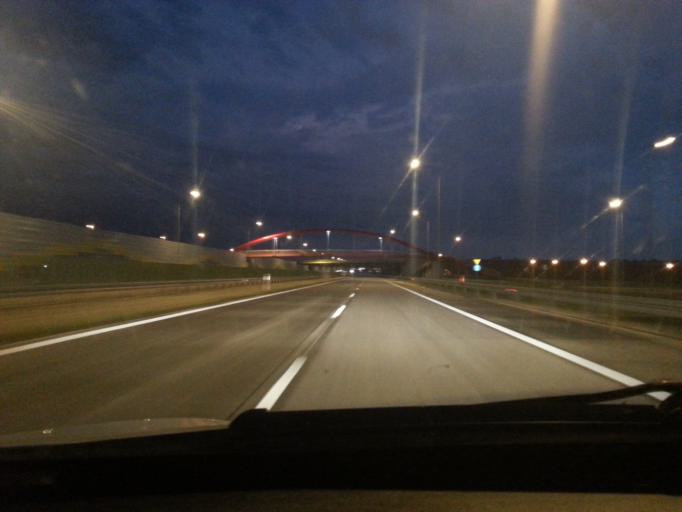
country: PL
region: Lodz Voivodeship
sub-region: Powiat wielunski
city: Czarnozyly
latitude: 51.3575
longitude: 18.5241
